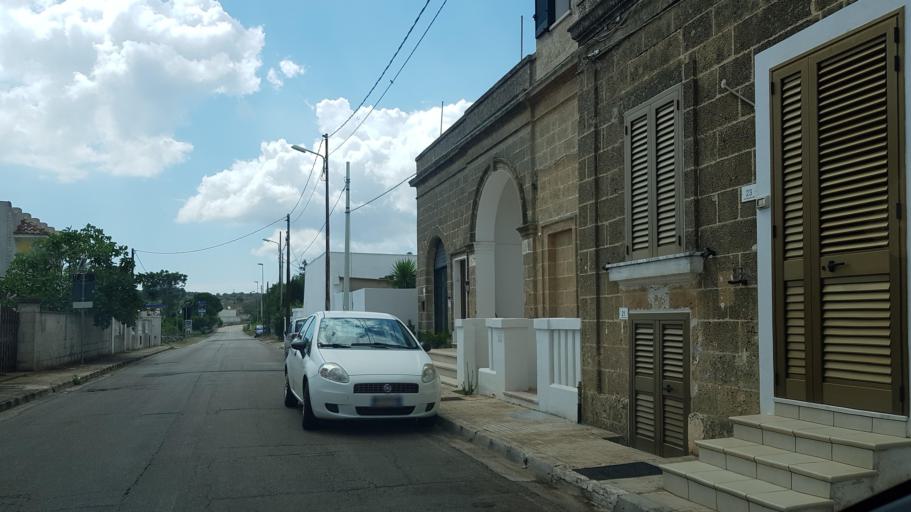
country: IT
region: Apulia
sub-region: Provincia di Lecce
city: Patu
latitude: 39.8433
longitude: 18.3340
